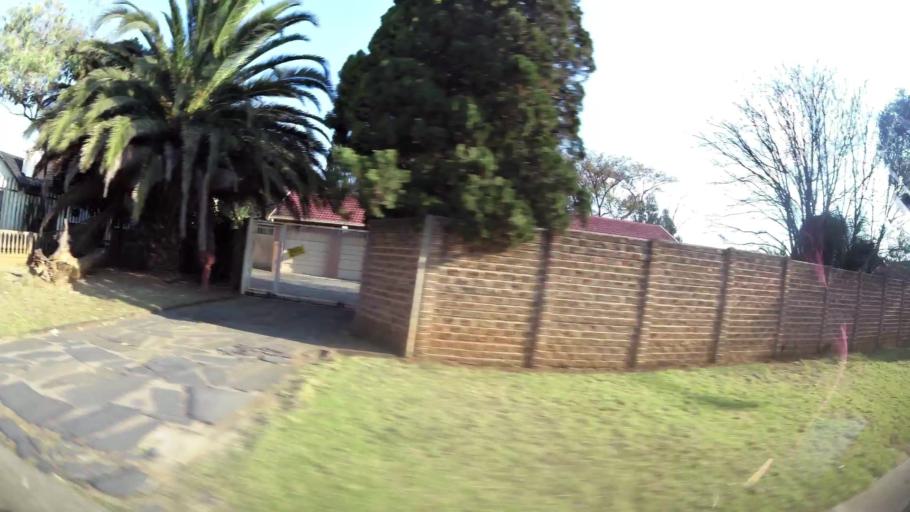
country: ZA
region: Gauteng
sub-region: Ekurhuleni Metropolitan Municipality
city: Benoni
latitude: -26.1324
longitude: 28.3709
